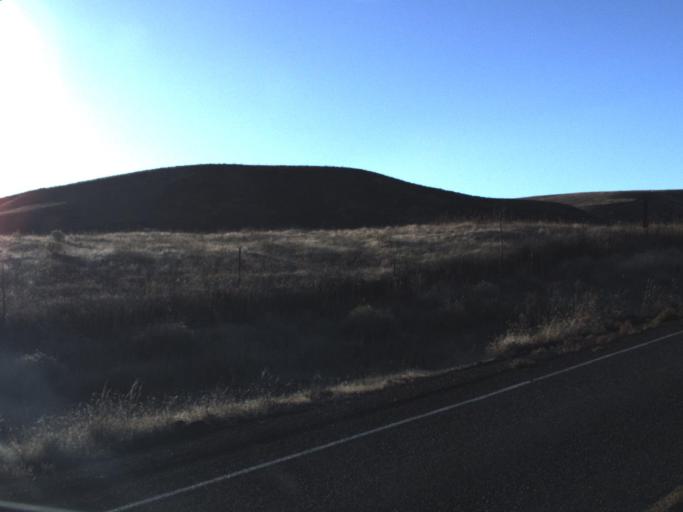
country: US
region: Washington
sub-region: Walla Walla County
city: Waitsburg
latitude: 46.6252
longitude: -118.2360
